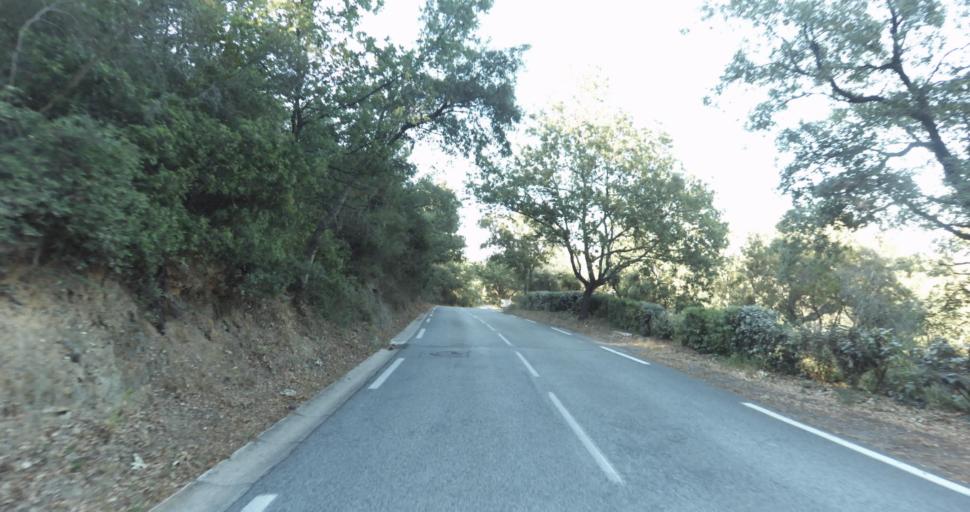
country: FR
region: Provence-Alpes-Cote d'Azur
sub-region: Departement du Var
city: Gassin
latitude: 43.2405
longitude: 6.5875
